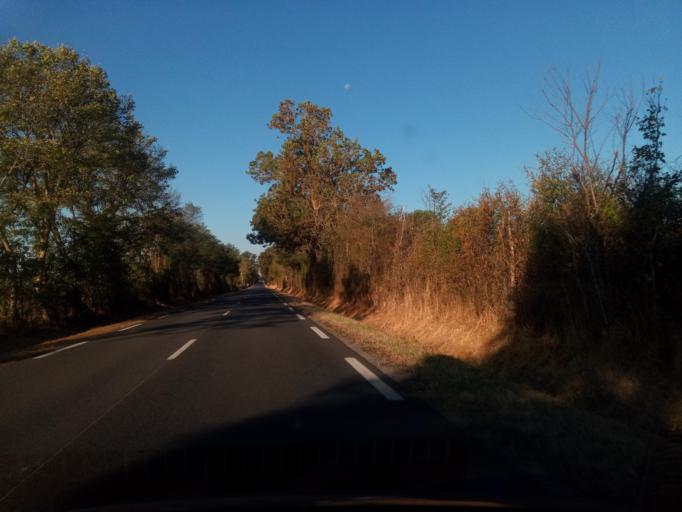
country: FR
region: Poitou-Charentes
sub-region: Departement de la Vienne
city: Montmorillon
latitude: 46.4129
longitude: 0.8235
